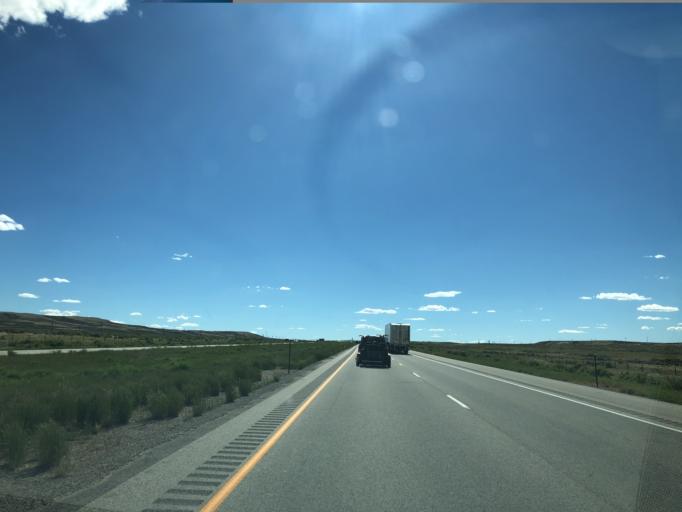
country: US
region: Wyoming
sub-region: Sweetwater County
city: Rock Springs
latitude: 41.6394
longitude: -108.2206
